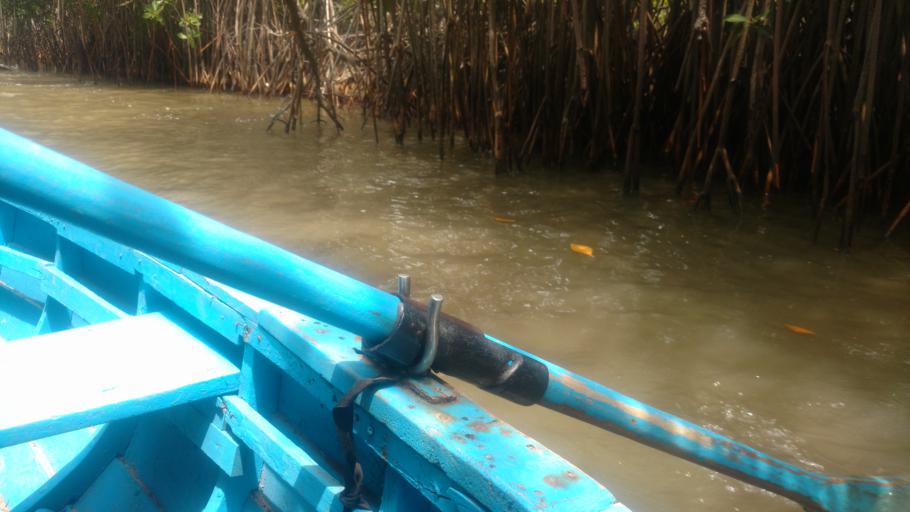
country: IN
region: Tamil Nadu
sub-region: Cuddalore
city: Annamalainagar
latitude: 11.4337
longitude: 79.7938
